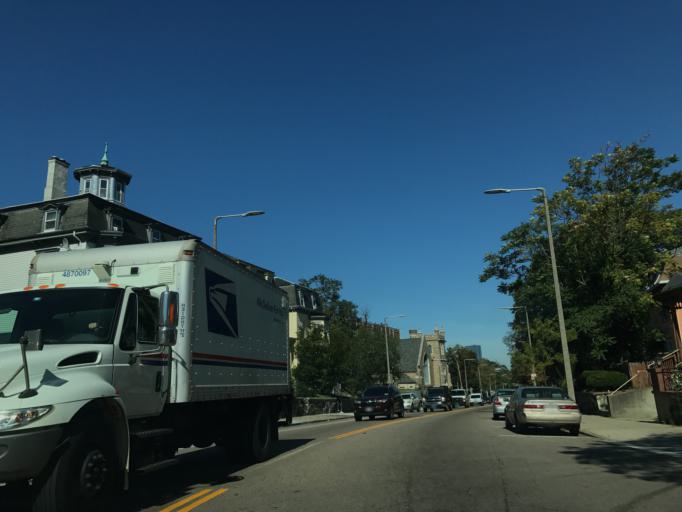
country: US
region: Massachusetts
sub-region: Suffolk County
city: Jamaica Plain
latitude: 42.3141
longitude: -71.0837
